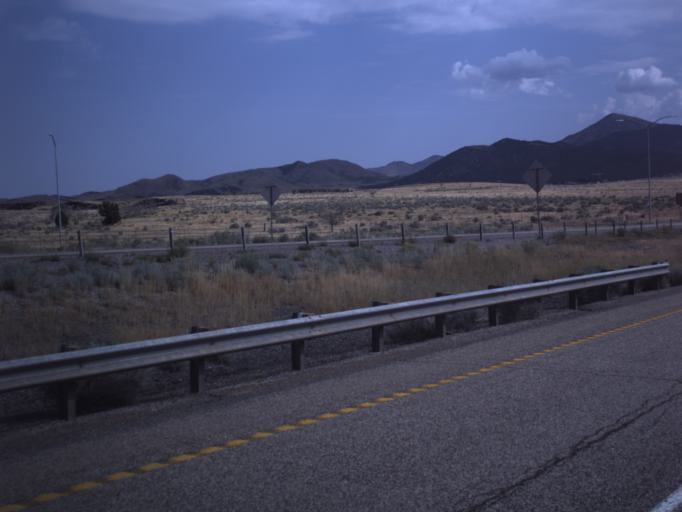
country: US
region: Utah
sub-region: Beaver County
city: Beaver
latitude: 38.5780
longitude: -112.6018
